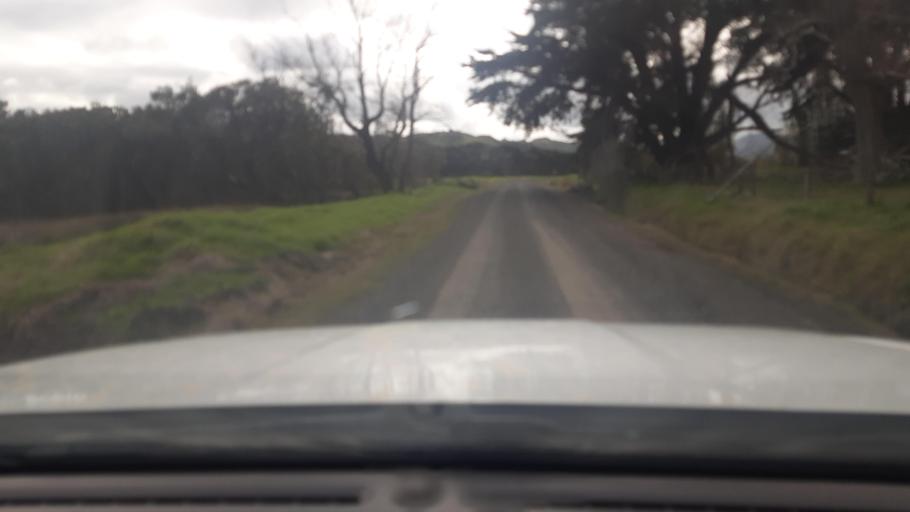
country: NZ
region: Northland
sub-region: Far North District
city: Ahipara
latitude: -35.3365
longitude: 173.2212
